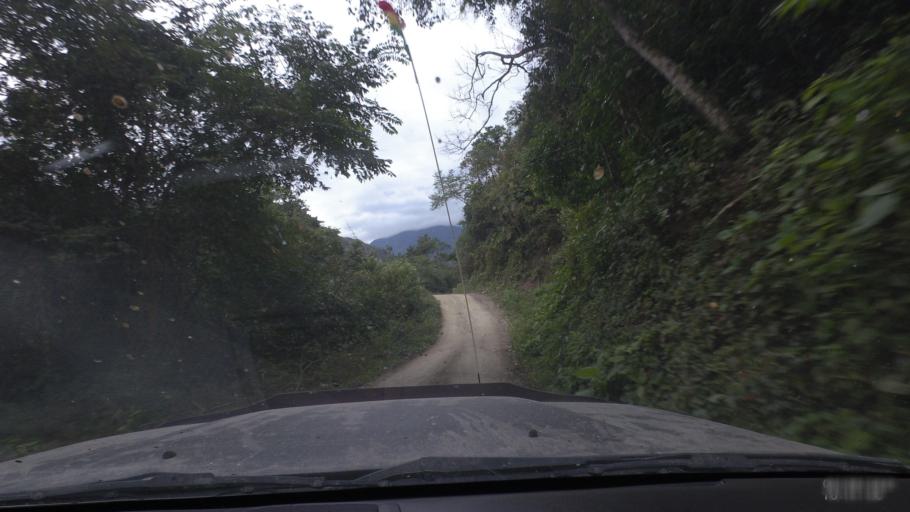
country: BO
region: La Paz
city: Quime
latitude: -16.5246
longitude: -66.7545
